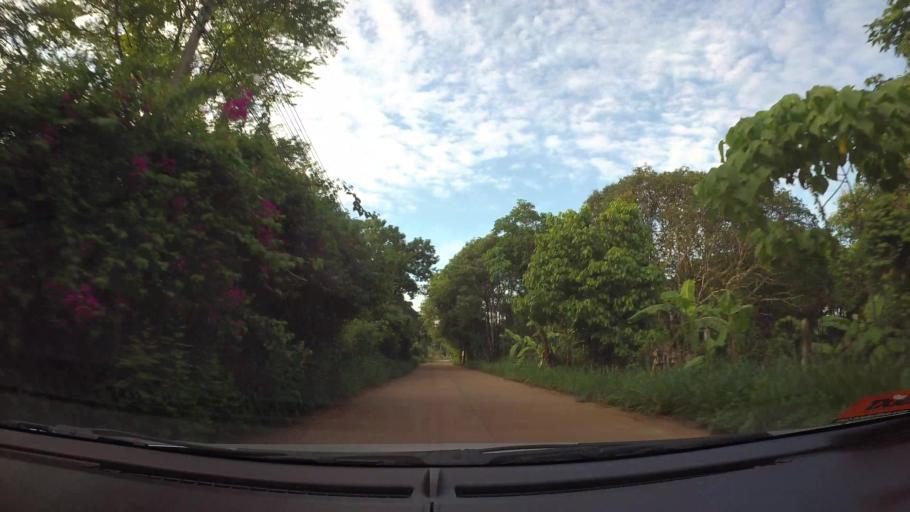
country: TH
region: Chon Buri
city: Sattahip
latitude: 12.7012
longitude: 100.9287
